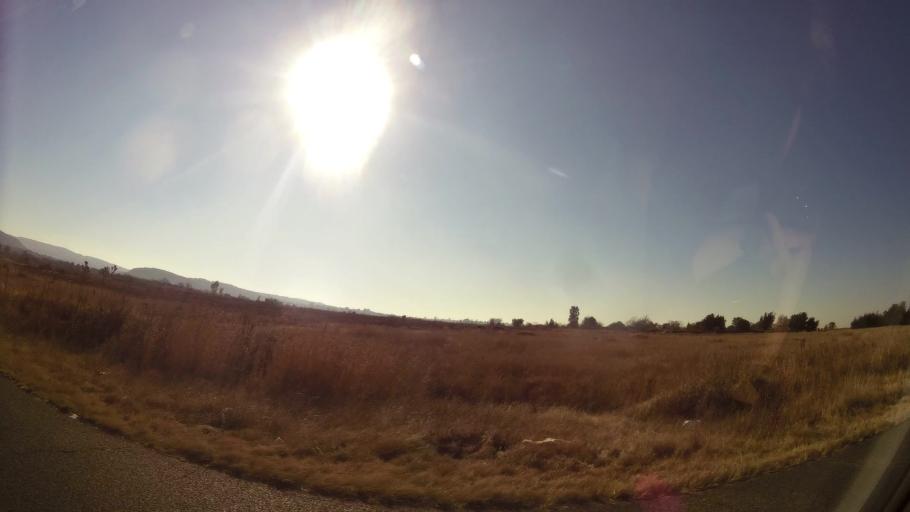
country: ZA
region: Gauteng
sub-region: City of Johannesburg Metropolitan Municipality
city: Johannesburg
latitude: -26.3228
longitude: 28.0673
